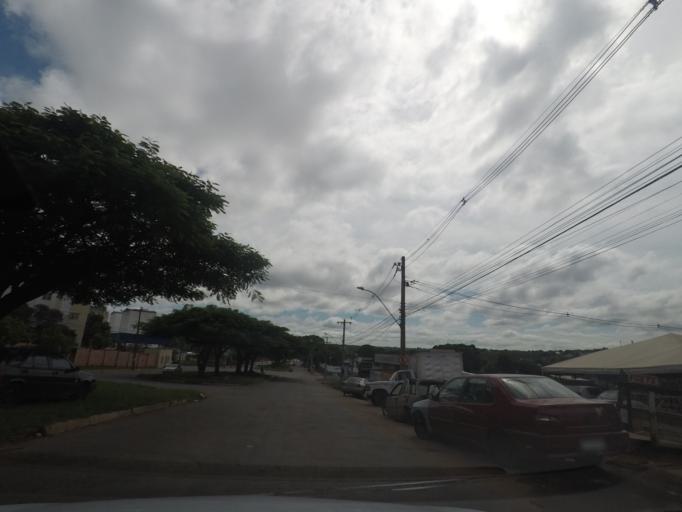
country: BR
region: Goias
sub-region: Goiania
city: Goiania
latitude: -16.6609
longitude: -49.2113
